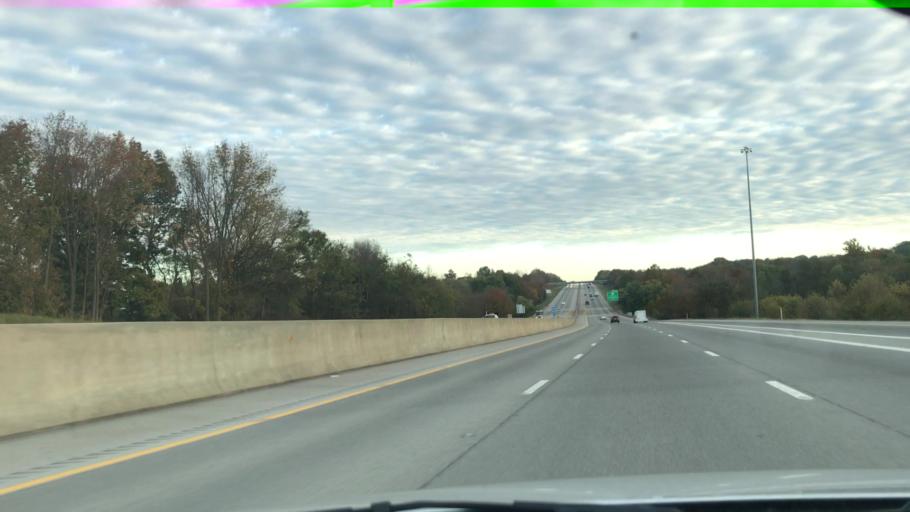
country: US
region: Kentucky
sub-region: Simpson County
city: Franklin
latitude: 36.6906
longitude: -86.5356
